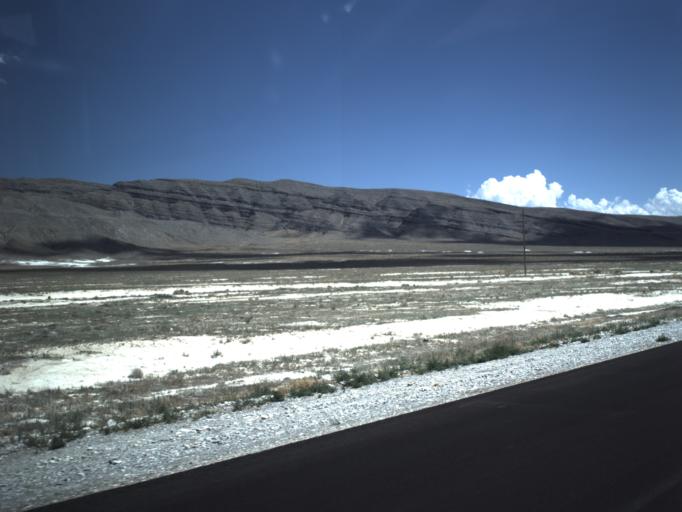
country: US
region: Utah
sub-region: Beaver County
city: Milford
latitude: 39.0640
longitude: -113.4451
